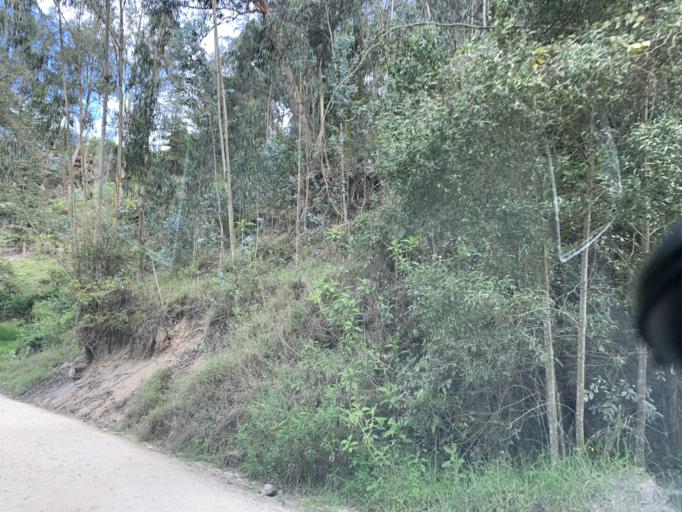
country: CO
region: Boyaca
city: Ramiriqui
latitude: 5.4119
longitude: -73.3281
